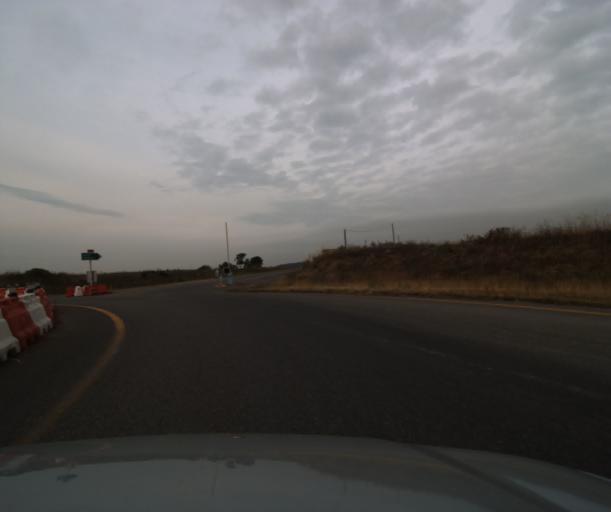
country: FR
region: Midi-Pyrenees
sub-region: Departement du Gers
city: Aubiet
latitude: 43.6494
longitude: 0.7369
